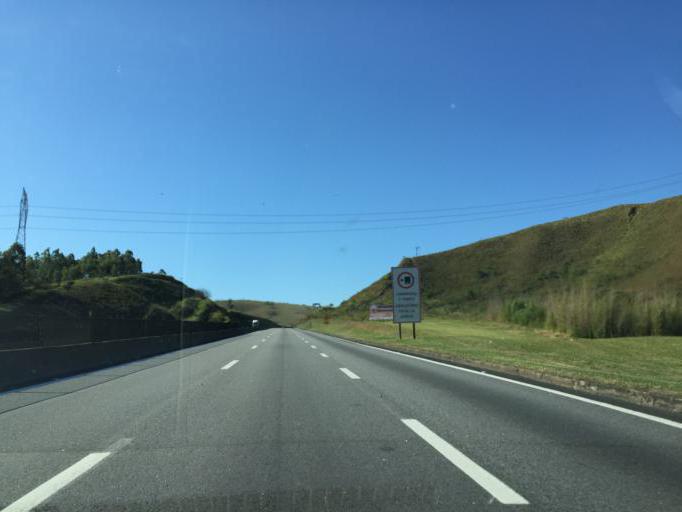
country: BR
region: Sao Paulo
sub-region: Cruzeiro
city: Cruzeiro
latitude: -22.6444
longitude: -44.9495
